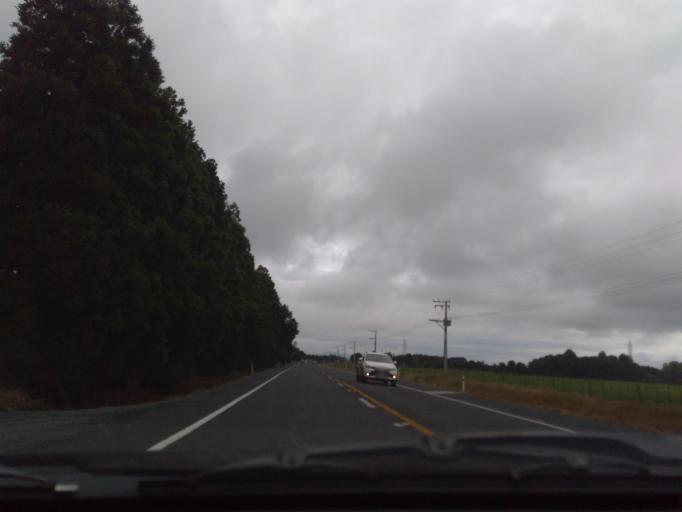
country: NZ
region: Northland
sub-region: Whangarei
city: Ruakaka
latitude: -35.9965
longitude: 174.4190
